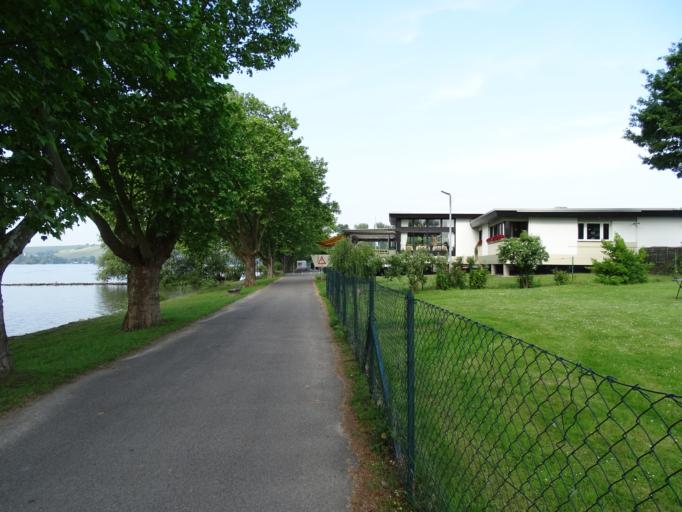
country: DE
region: Hesse
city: Geisenheim
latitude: 49.9791
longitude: 7.9585
